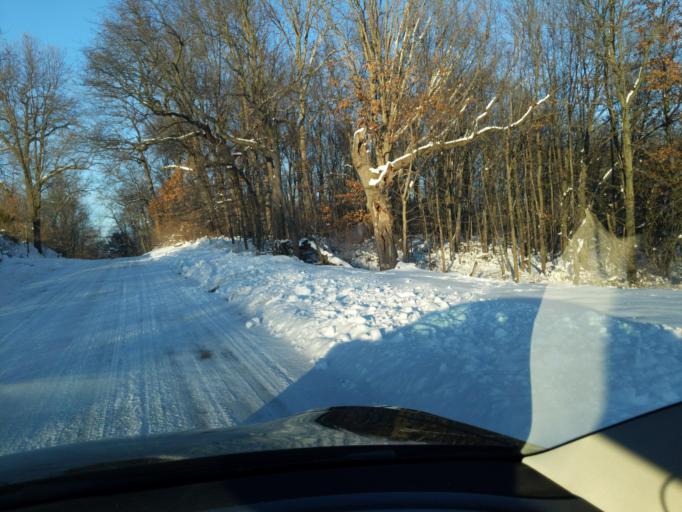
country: US
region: Michigan
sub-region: Ingham County
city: Stockbridge
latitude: 42.5081
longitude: -84.1178
